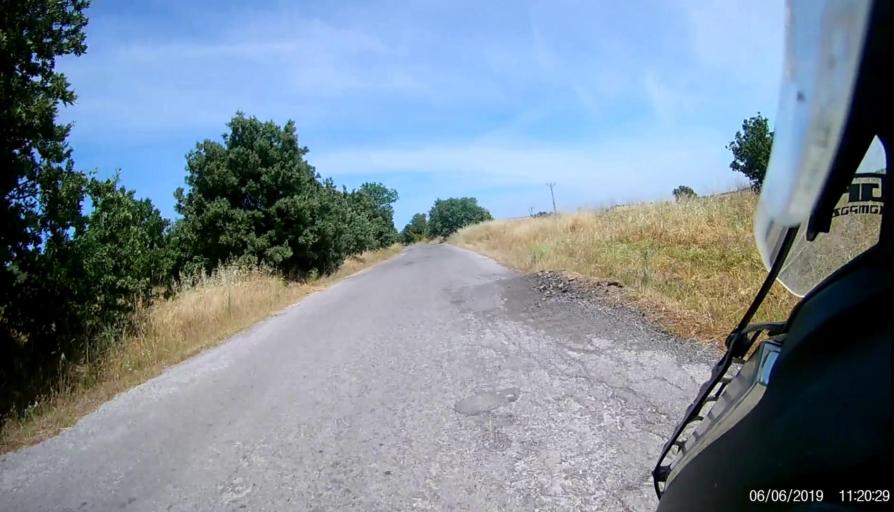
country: TR
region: Canakkale
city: Gulpinar
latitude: 39.6670
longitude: 26.1635
